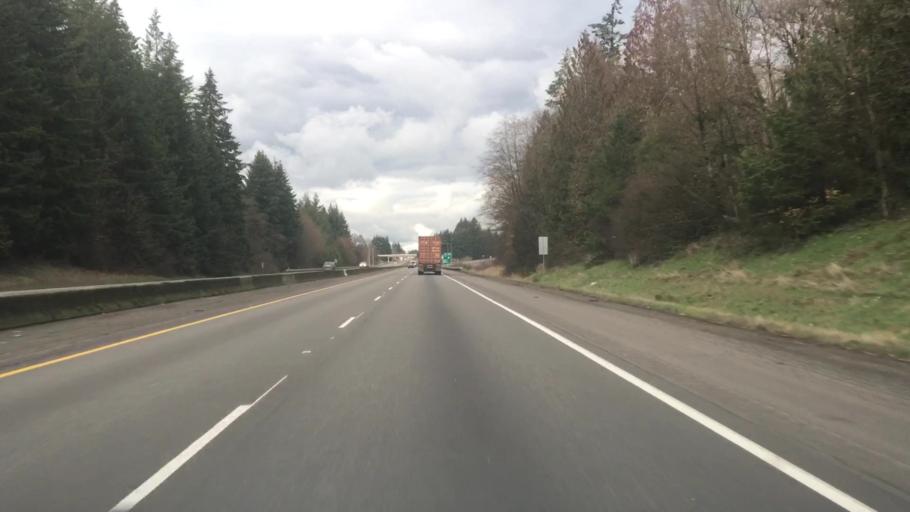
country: US
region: Washington
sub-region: Lewis County
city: Napavine
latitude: 46.5400
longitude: -122.8765
